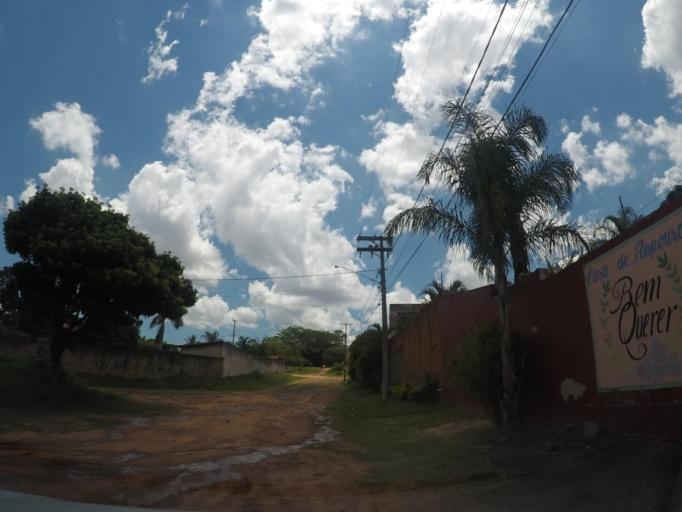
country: BR
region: Sao Paulo
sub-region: Hortolandia
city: Hortolandia
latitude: -22.8426
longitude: -47.2316
